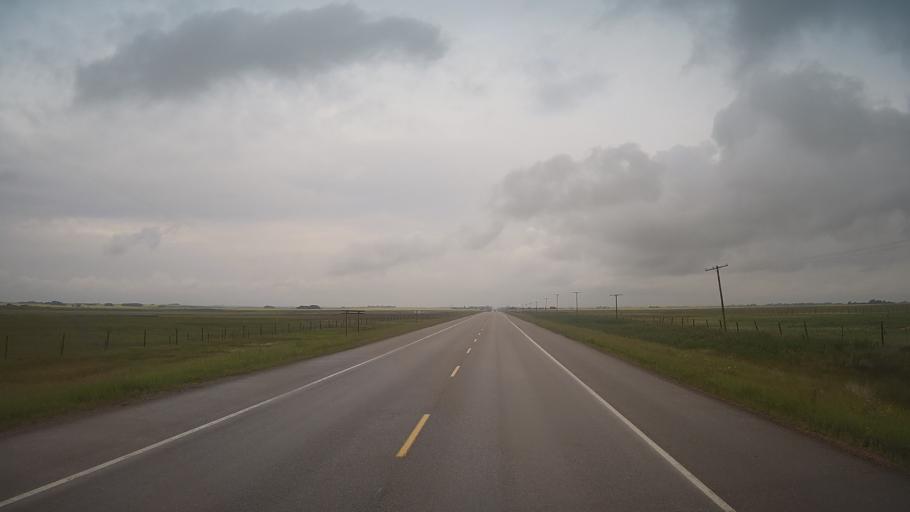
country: CA
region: Saskatchewan
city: Unity
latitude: 52.4349
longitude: -108.9796
